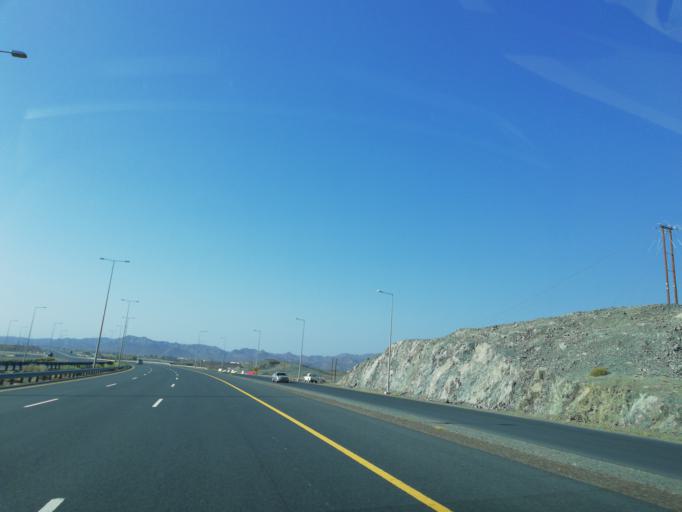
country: OM
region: Muhafazat ad Dakhiliyah
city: Sufalat Sama'il
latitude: 23.0591
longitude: 58.1910
